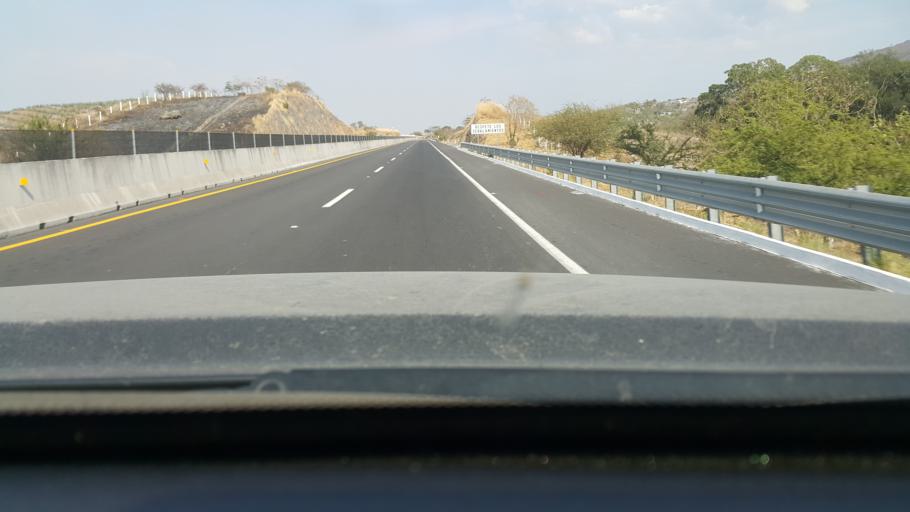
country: MX
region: Nayarit
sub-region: Ahuacatlan
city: Ahuacatlan
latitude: 21.0568
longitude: -104.5284
